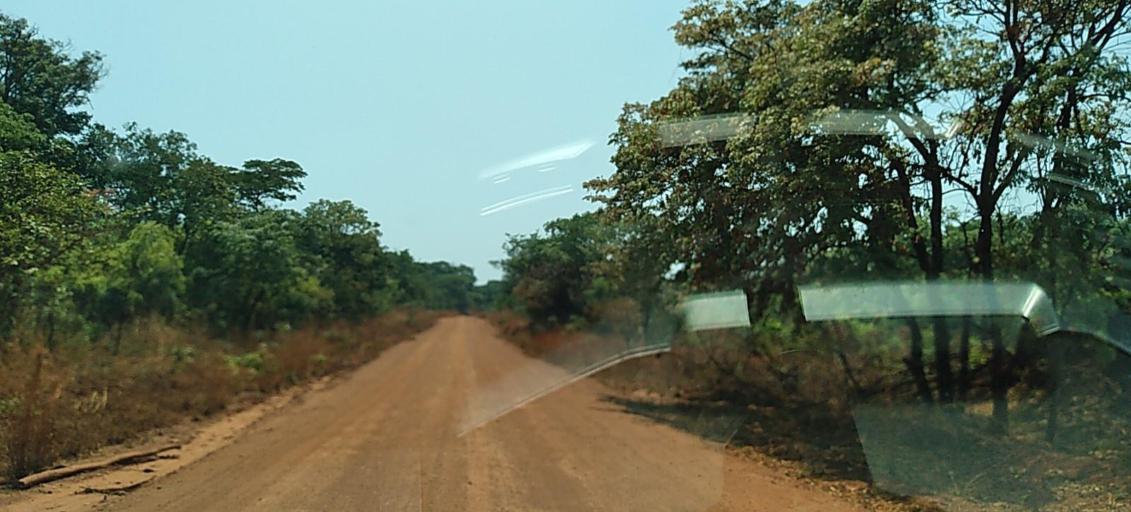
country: ZM
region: North-Western
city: Kansanshi
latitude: -11.9843
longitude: 26.8576
